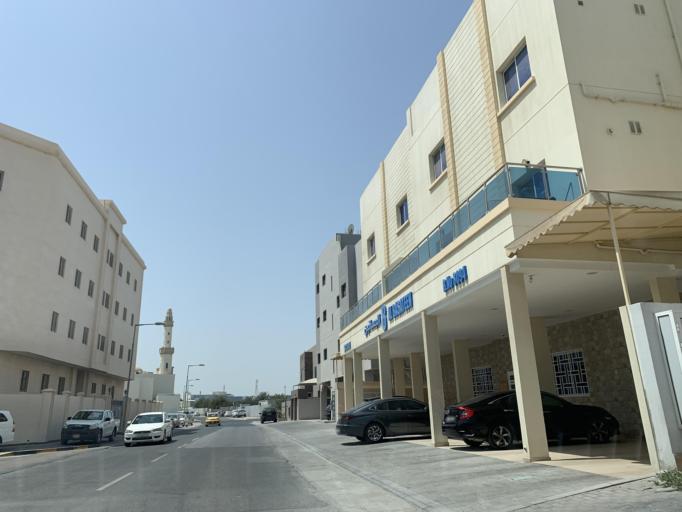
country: BH
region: Northern
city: Madinat `Isa
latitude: 26.1888
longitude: 50.5448
